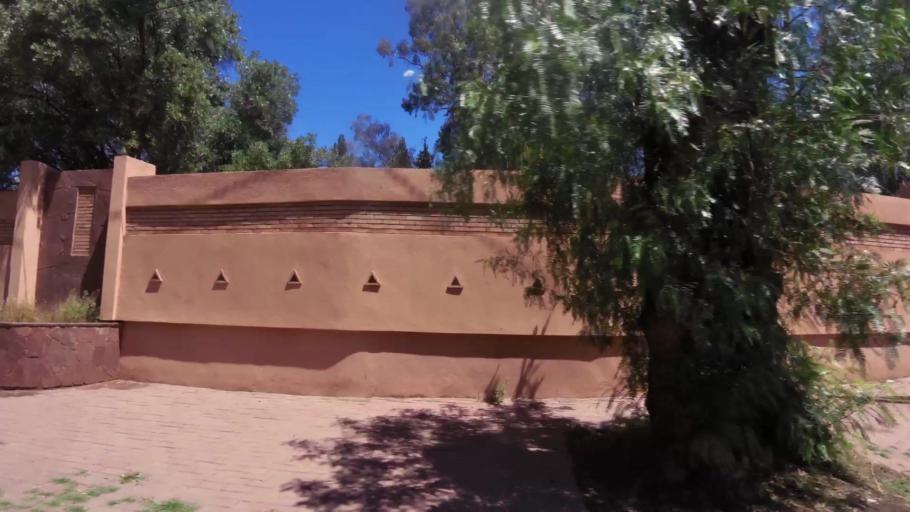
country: MA
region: Marrakech-Tensift-Al Haouz
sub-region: Marrakech
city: Marrakesh
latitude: 31.6246
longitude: -8.0107
